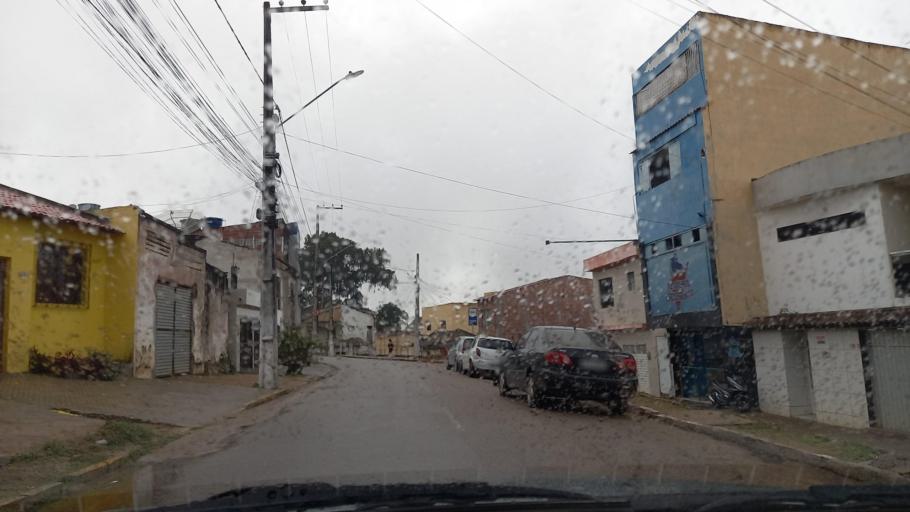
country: BR
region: Pernambuco
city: Garanhuns
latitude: -8.8869
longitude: -36.4999
